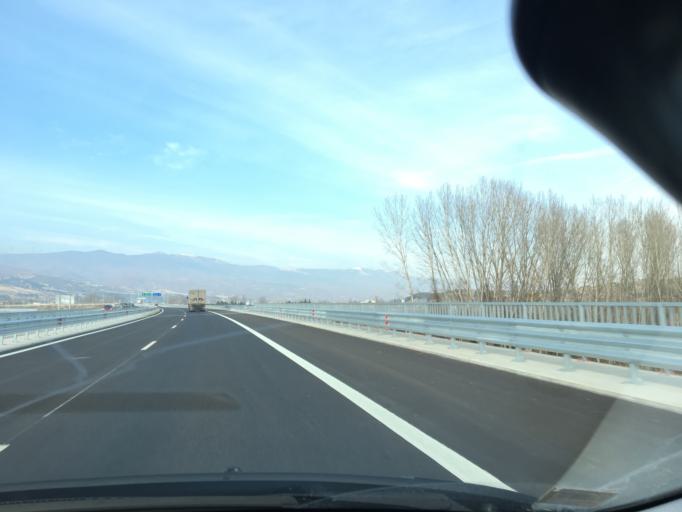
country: BG
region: Blagoevgrad
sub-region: Obshtina Strumyani
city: Strumyani
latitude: 41.6239
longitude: 23.2124
